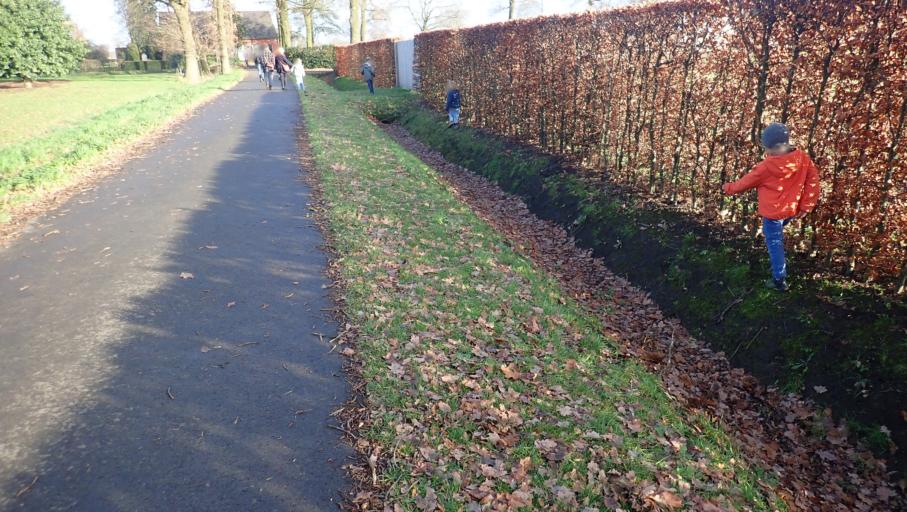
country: BE
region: Flanders
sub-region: Provincie Antwerpen
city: Brecht
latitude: 51.3579
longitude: 4.6500
